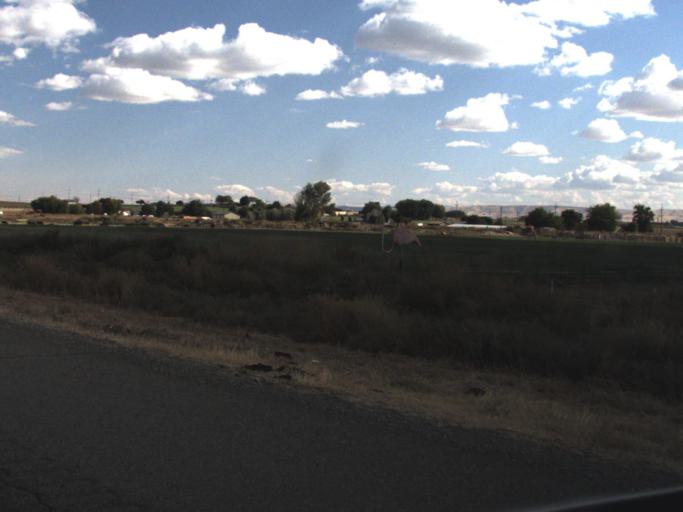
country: US
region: Washington
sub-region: Yakima County
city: Sunnyside
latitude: 46.3059
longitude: -119.9958
